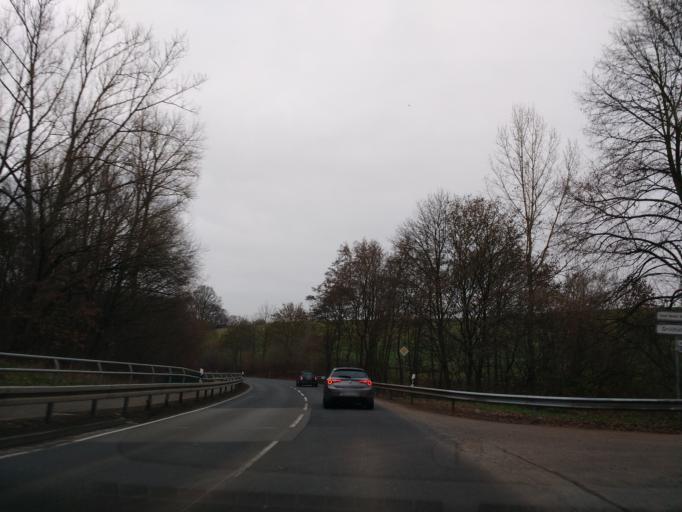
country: DE
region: Hesse
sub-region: Regierungsbezirk Kassel
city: Guxhagen
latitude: 51.2118
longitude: 9.4358
